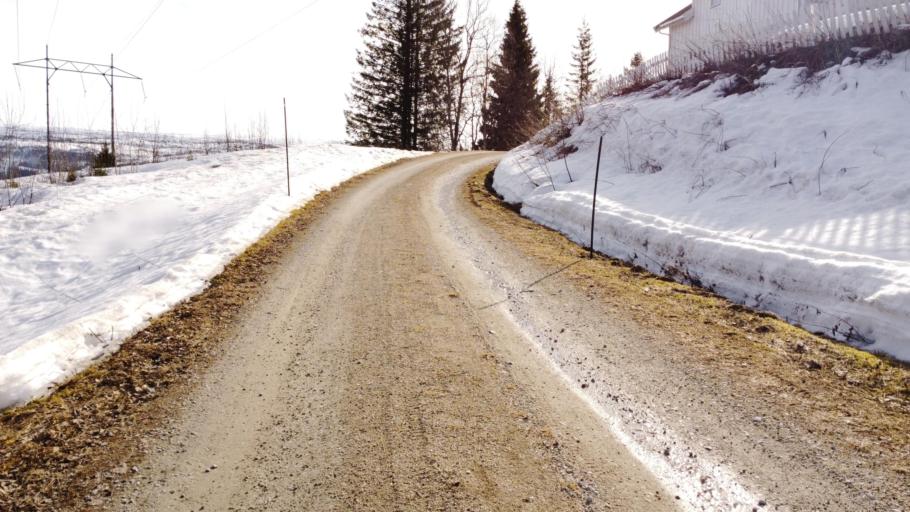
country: NO
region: Nordland
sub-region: Rana
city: Mo i Rana
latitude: 66.3311
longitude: 14.1650
